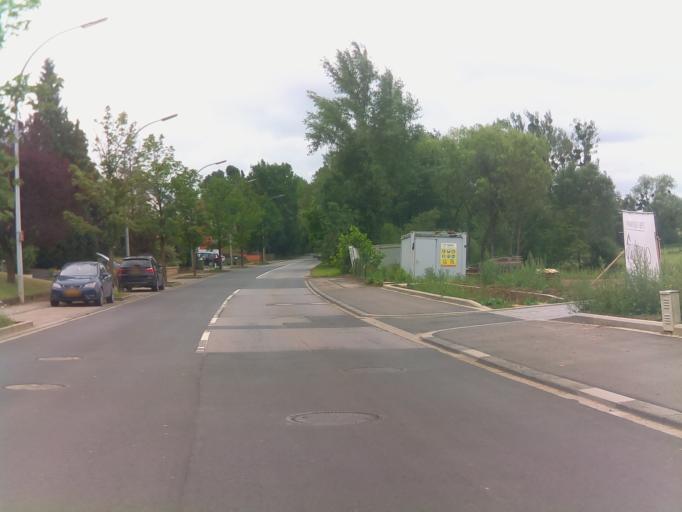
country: LU
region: Luxembourg
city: Pontpierre
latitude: 49.5447
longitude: 6.0170
